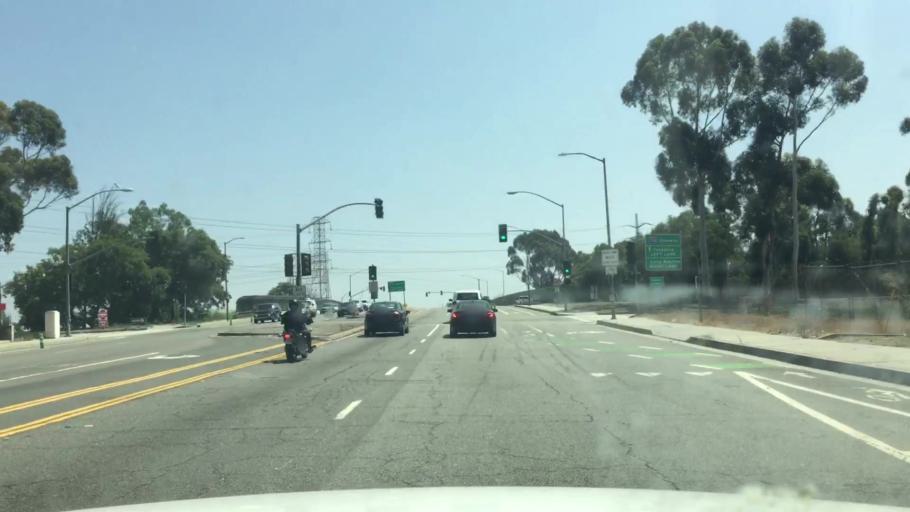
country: US
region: California
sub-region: Los Angeles County
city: East Rancho Dominguez
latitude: 33.8644
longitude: -118.1999
